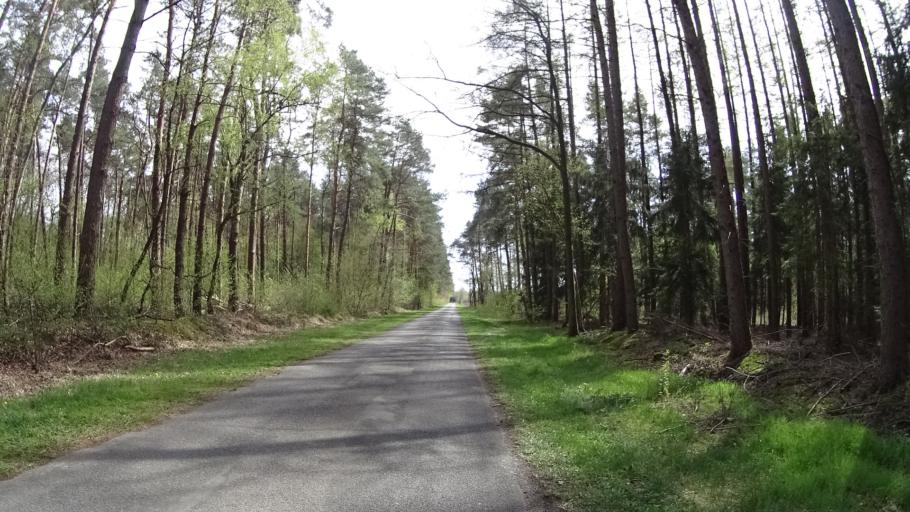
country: DE
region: Lower Saxony
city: Lunne
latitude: 52.3803
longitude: 7.3979
